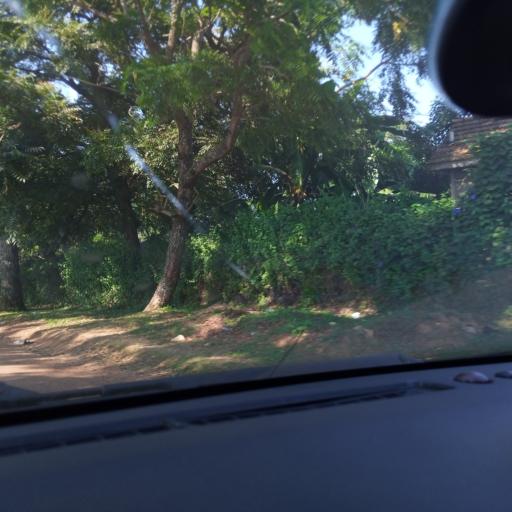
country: UG
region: Central Region
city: Masaka
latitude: -0.3378
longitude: 31.7356
